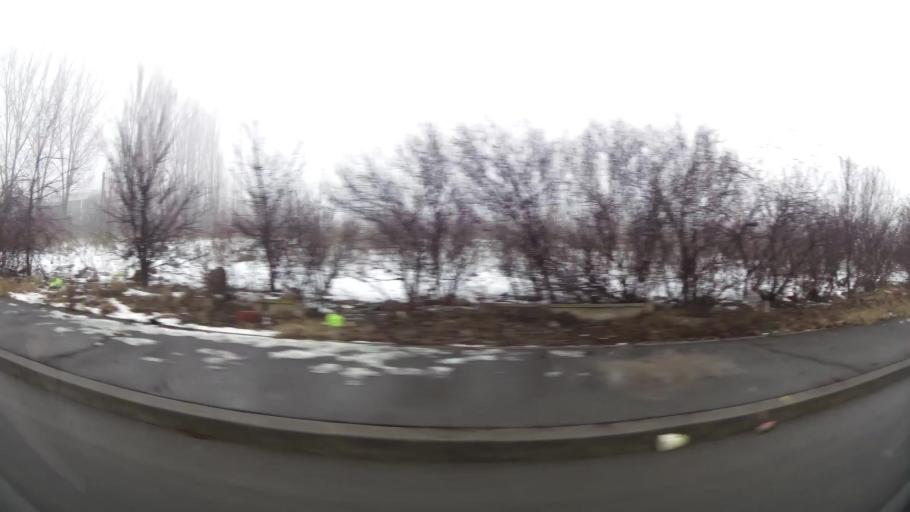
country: RO
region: Ilfov
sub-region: Comuna Chiajna
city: Rosu
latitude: 44.4757
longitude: 26.0095
